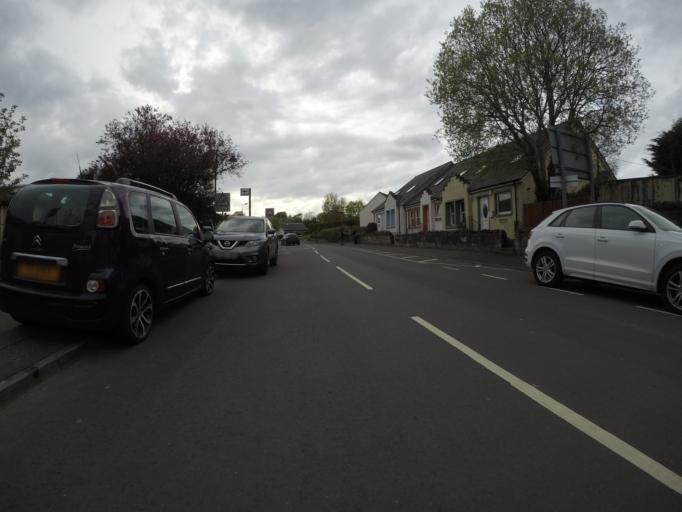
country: GB
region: Scotland
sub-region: East Ayrshire
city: Kilmaurs
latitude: 55.6385
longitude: -4.5274
